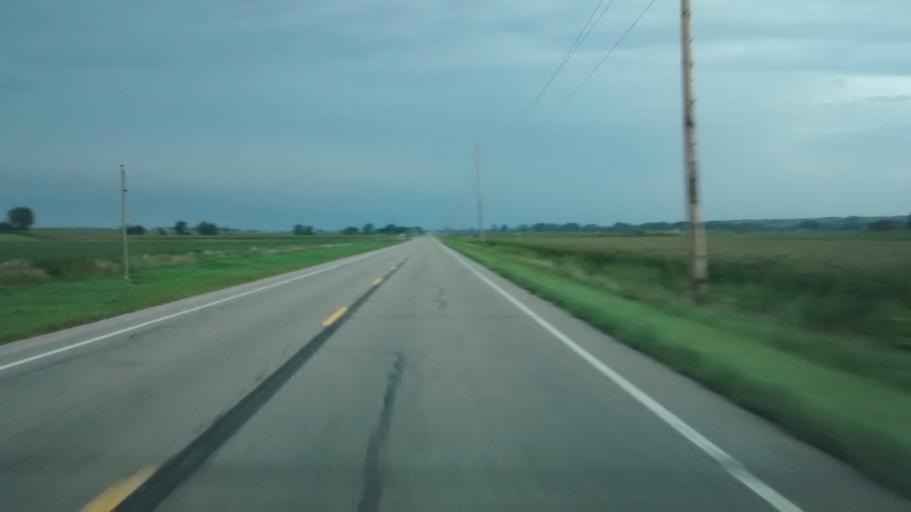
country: US
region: Iowa
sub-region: Plymouth County
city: Kingsley
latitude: 42.5507
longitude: -96.0199
